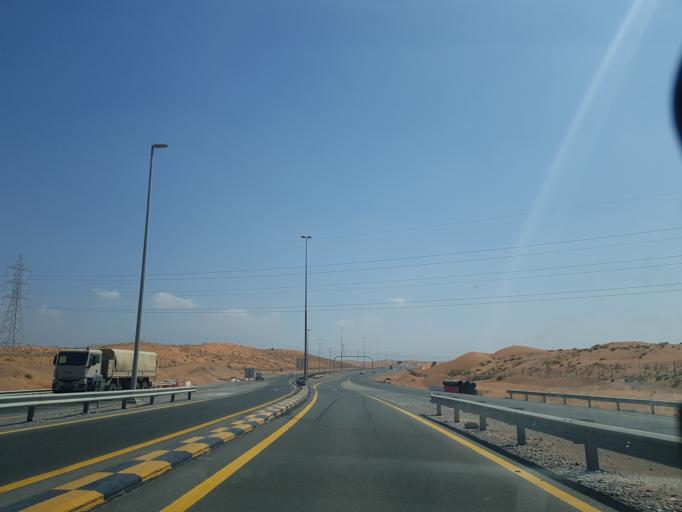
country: AE
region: Ra's al Khaymah
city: Ras al-Khaimah
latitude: 25.6706
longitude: 55.8821
